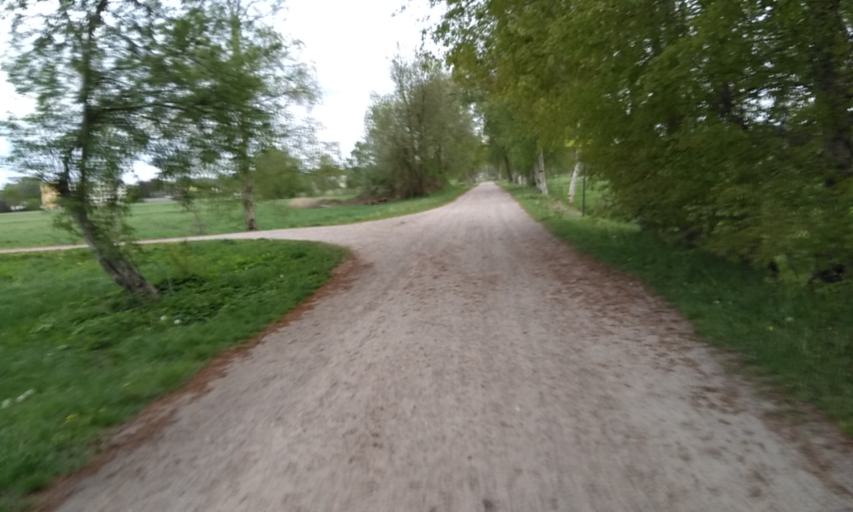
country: DE
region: Lower Saxony
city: Buxtehude
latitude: 53.4795
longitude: 9.6763
